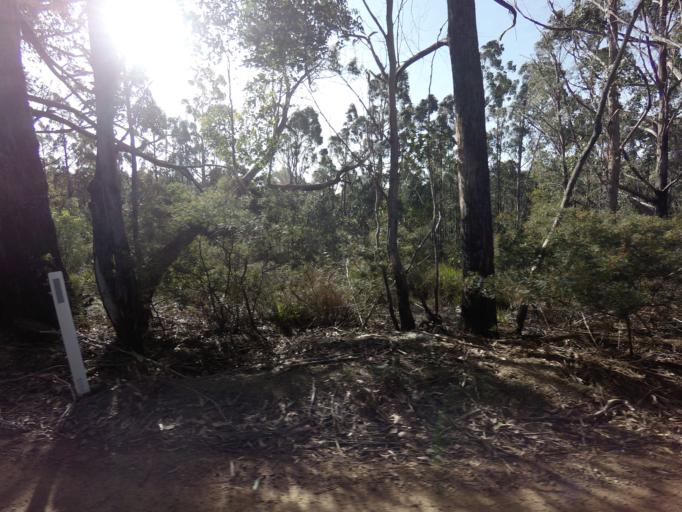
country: AU
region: Tasmania
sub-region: Kingborough
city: Kettering
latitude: -43.0976
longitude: 147.2628
